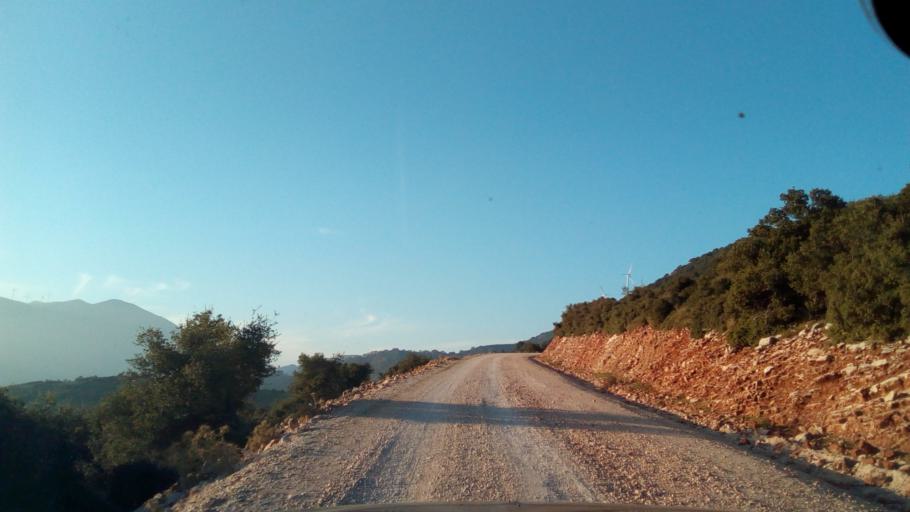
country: GR
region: West Greece
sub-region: Nomos Aitolias kai Akarnanias
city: Nafpaktos
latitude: 38.4382
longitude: 21.8483
